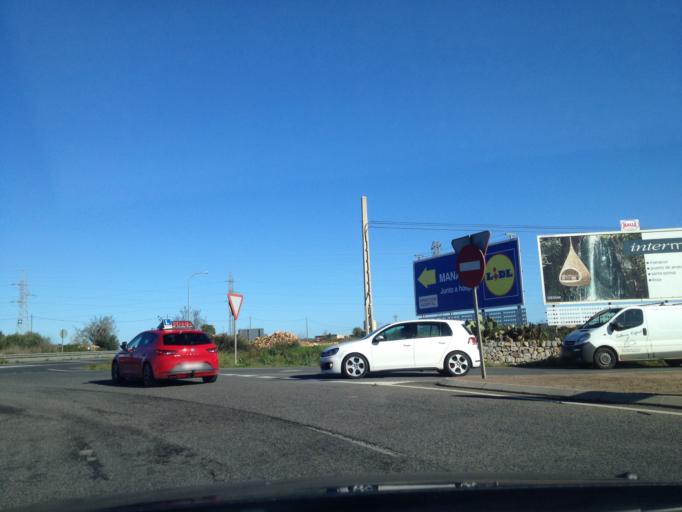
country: ES
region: Balearic Islands
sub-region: Illes Balears
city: Manacor
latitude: 39.5729
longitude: 3.1872
